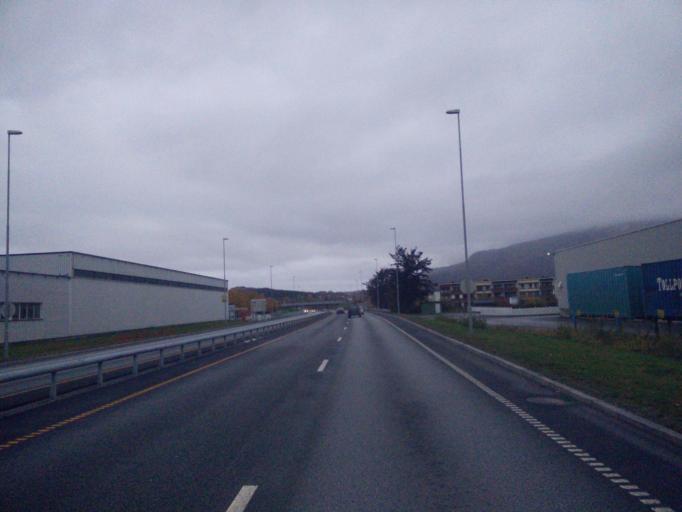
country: NO
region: Nord-Trondelag
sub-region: Stjordal
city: Stjordal
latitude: 63.4763
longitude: 10.9031
